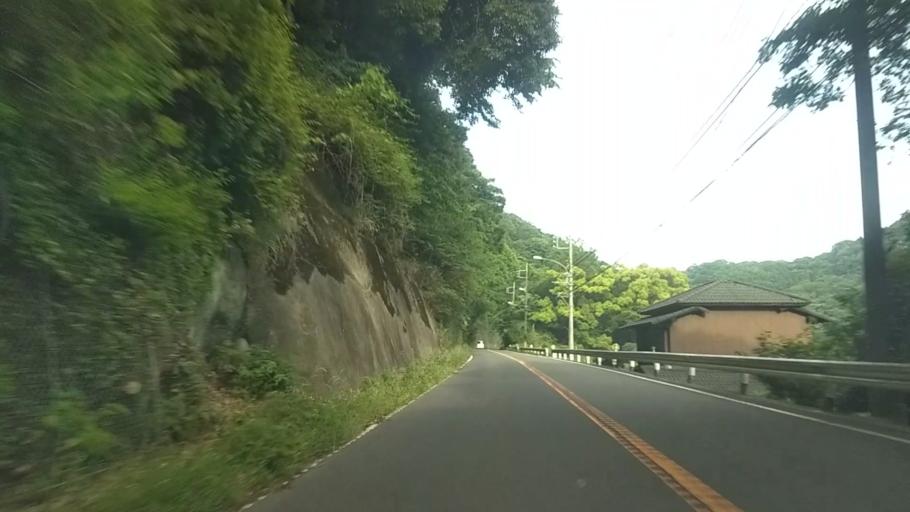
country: JP
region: Shizuoka
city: Gotemba
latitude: 35.3610
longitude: 139.0573
